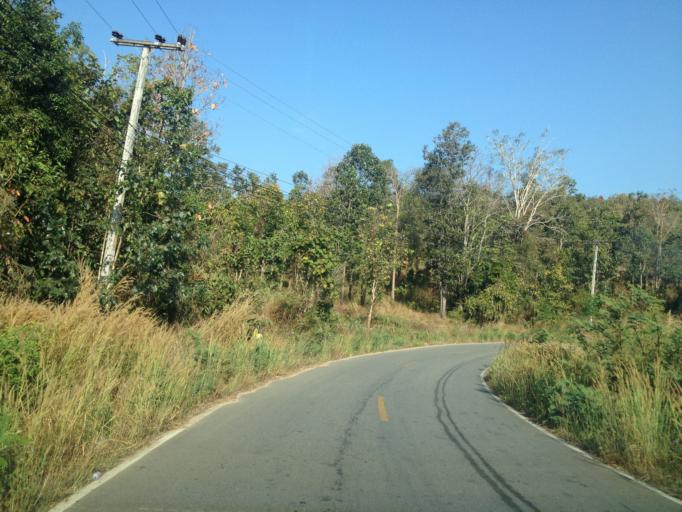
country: TH
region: Mae Hong Son
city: Ban Huai I Huak
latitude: 18.1155
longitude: 98.2173
